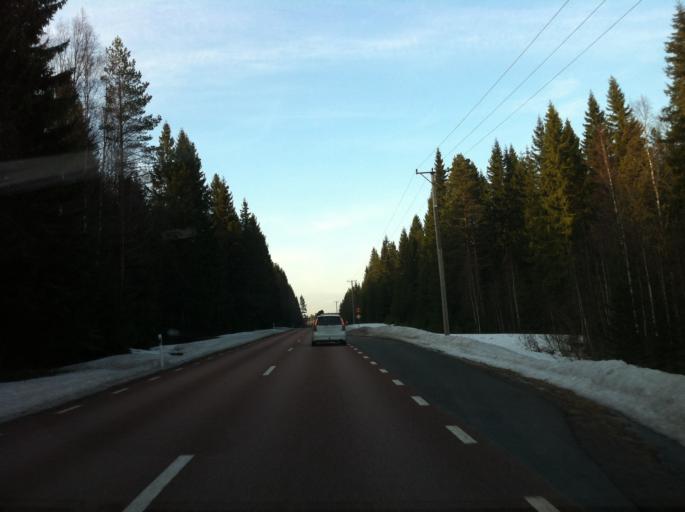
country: SE
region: Vaermland
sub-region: Filipstads Kommun
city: Lesjofors
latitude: 60.2112
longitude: 14.1876
